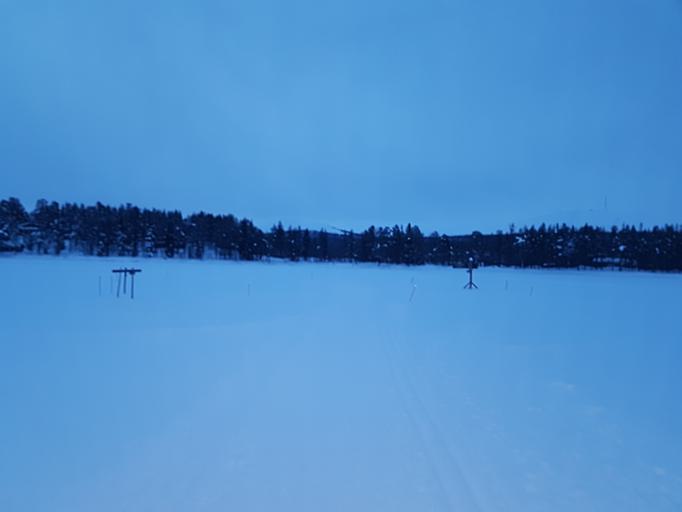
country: FI
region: Lapland
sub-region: Tunturi-Lappi
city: Kolari
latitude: 67.6085
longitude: 24.1688
